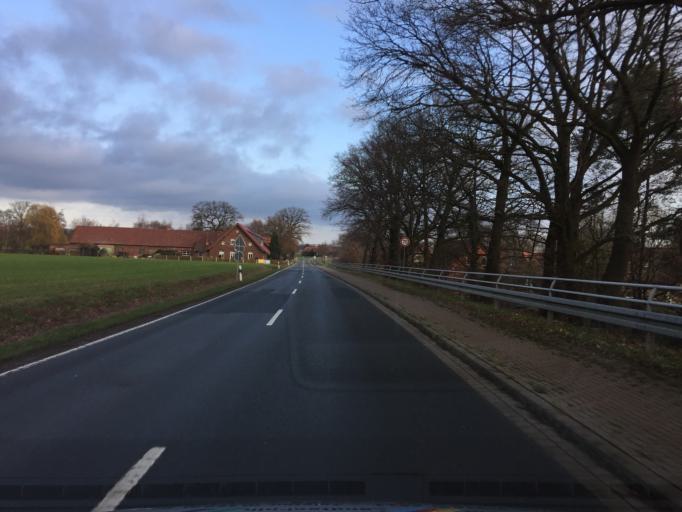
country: DE
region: Lower Saxony
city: Raddestorf
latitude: 52.4542
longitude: 8.9523
